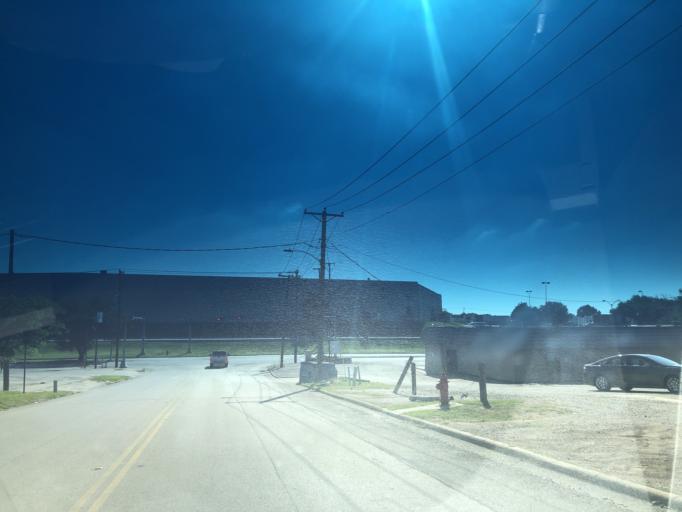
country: US
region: Texas
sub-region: Dallas County
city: Grand Prairie
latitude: 32.7274
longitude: -97.0452
